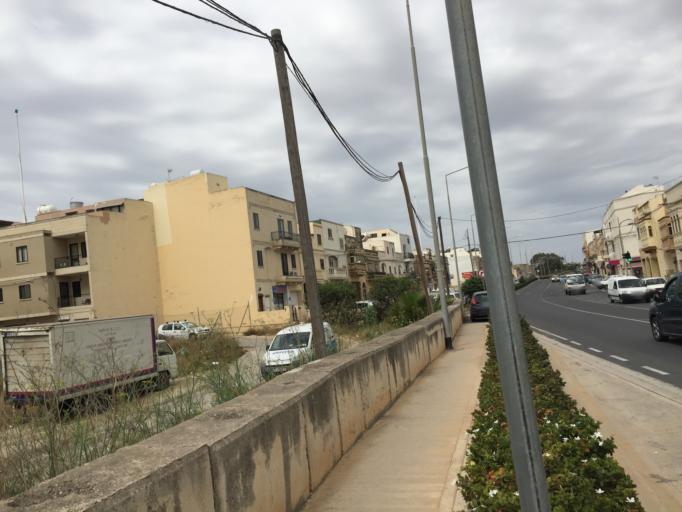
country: MT
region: Haz-Zabbar
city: Zabbar
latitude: 35.8711
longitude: 14.5370
